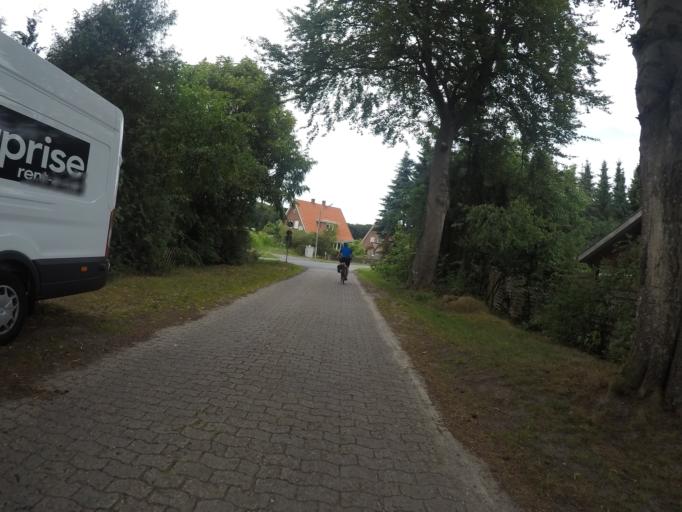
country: DE
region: Lower Saxony
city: Wingst
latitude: 53.7118
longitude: 9.0673
